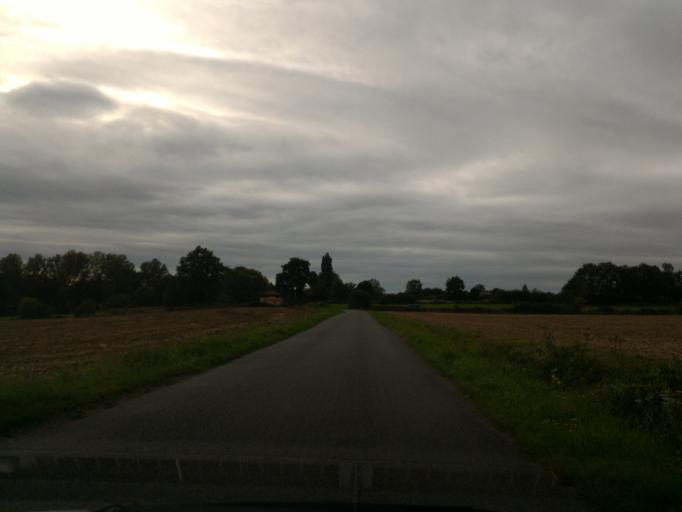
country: FR
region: Poitou-Charentes
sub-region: Departement de la Charente
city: Brigueuil
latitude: 45.9278
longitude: 0.8310
